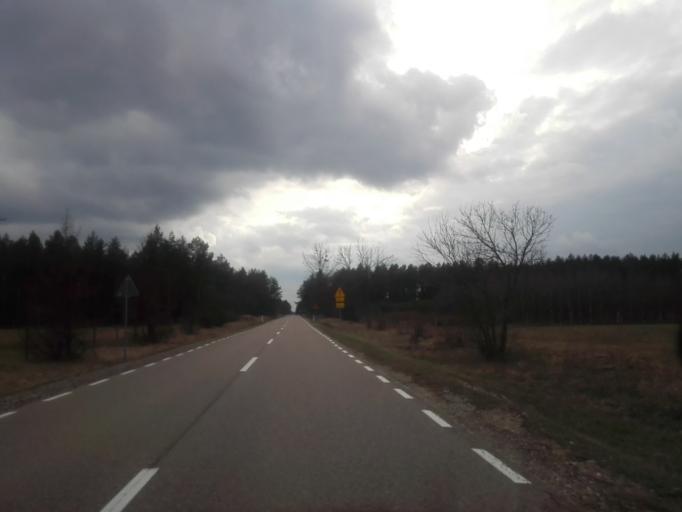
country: PL
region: Podlasie
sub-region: Powiat sejnenski
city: Krasnopol
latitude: 53.9540
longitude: 23.2115
